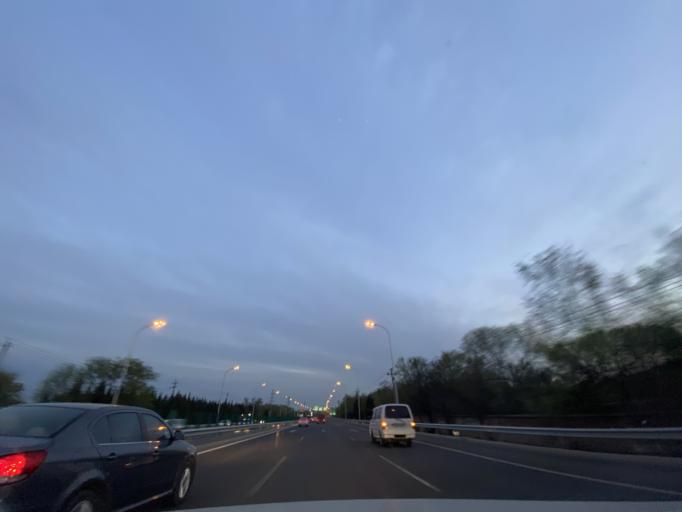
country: CN
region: Beijing
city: Xiangshan
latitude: 39.9859
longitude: 116.2150
